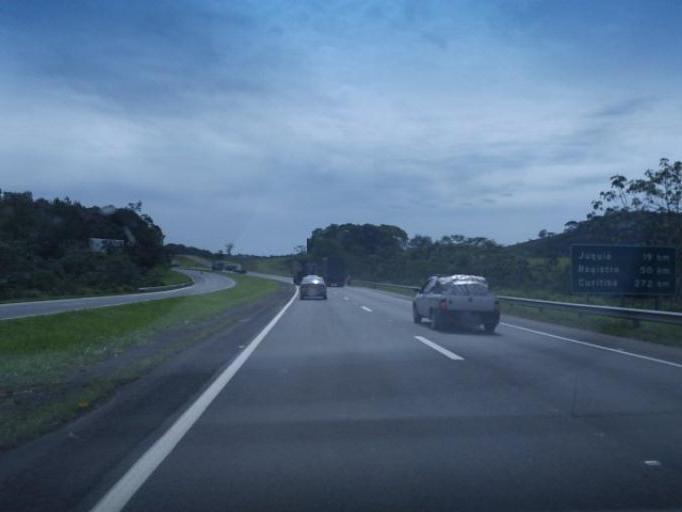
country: BR
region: Sao Paulo
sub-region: Miracatu
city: Miracatu
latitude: -24.2929
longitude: -47.4754
